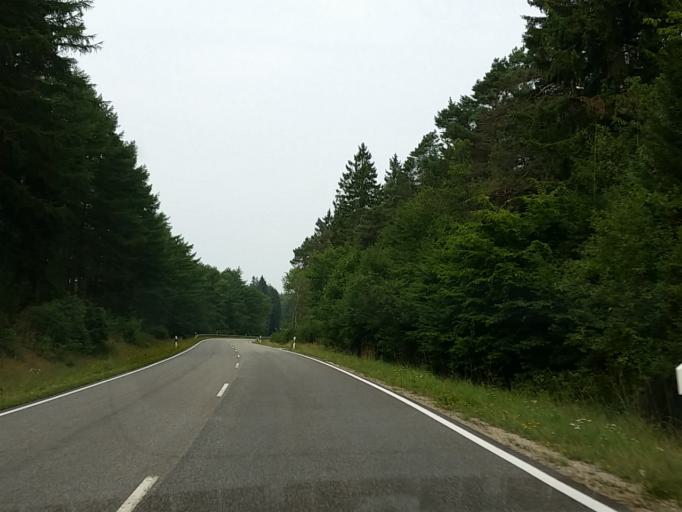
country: DE
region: Rheinland-Pfalz
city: Lorscheid
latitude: 49.7046
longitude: 6.8447
